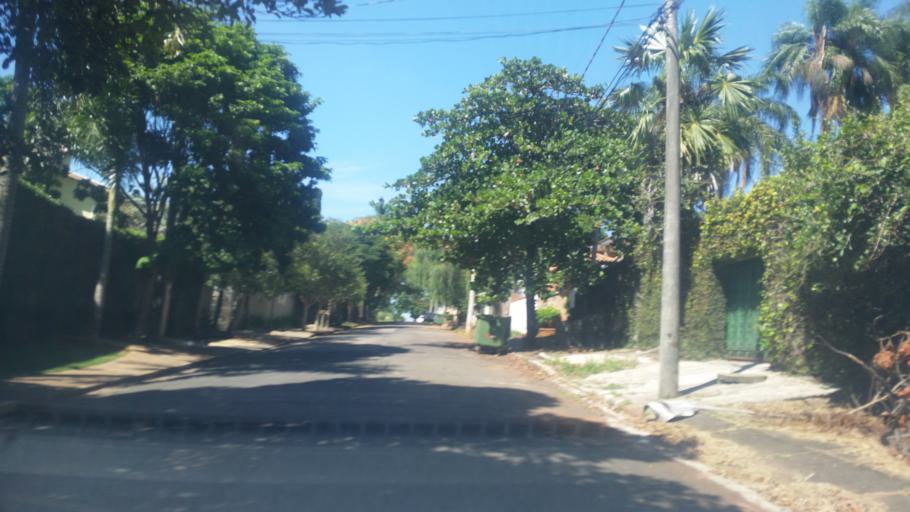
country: BR
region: Sao Paulo
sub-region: Campinas
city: Campinas
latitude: -22.8591
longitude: -47.0494
